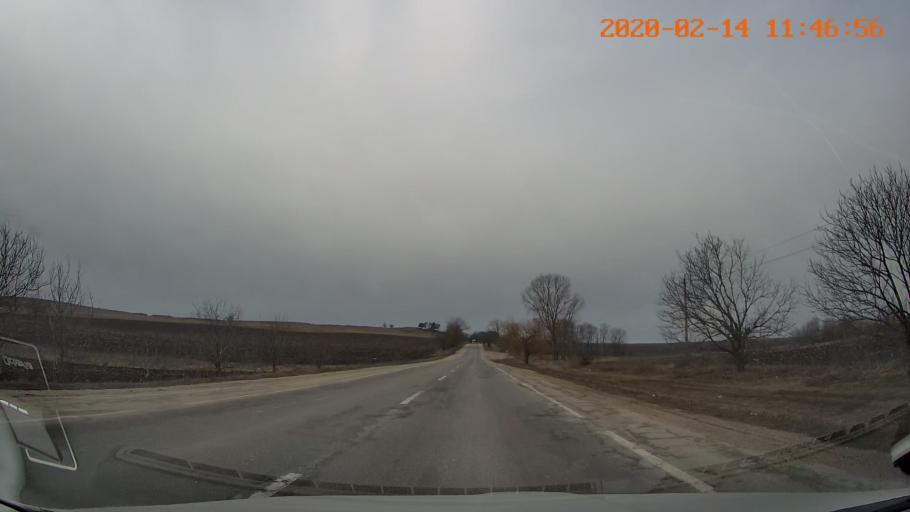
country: MD
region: Briceni
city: Briceni
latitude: 48.3165
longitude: 26.9810
